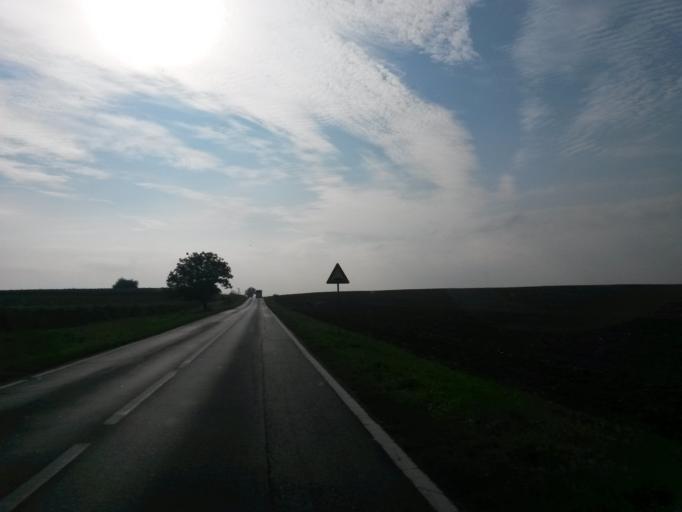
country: HR
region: Vukovarsko-Srijemska
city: Vukovar
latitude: 45.3161
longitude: 19.0715
